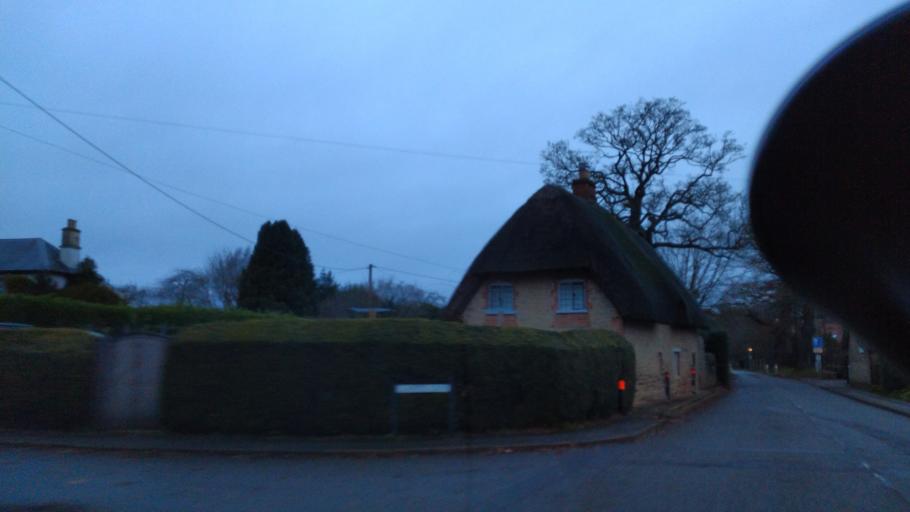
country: GB
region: England
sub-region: Oxfordshire
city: Shrivenham
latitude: 51.6004
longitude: -1.6515
